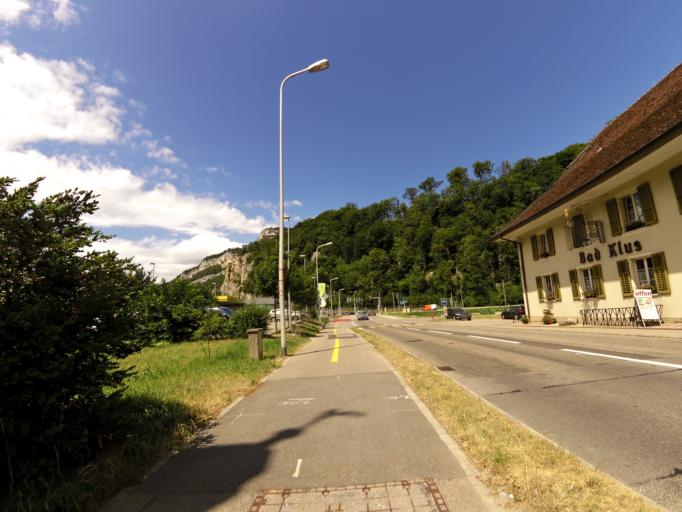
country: CH
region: Solothurn
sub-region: Bezirk Gaeu
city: Oensingen
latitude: 47.2959
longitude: 7.7046
